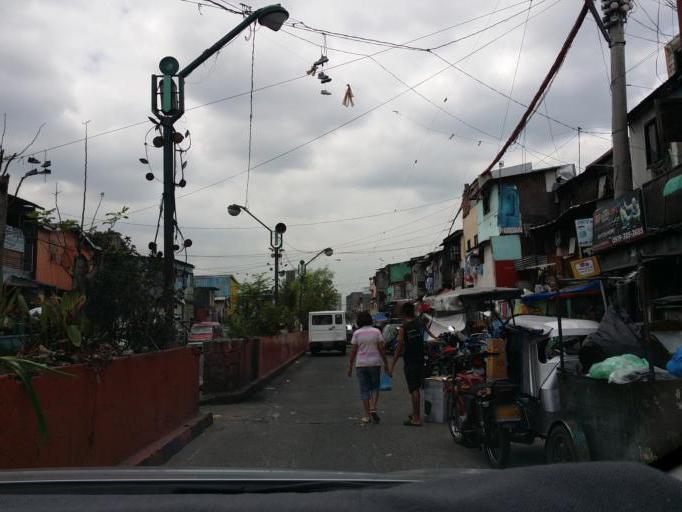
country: PH
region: Metro Manila
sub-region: Makati City
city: Makati City
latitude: 14.5713
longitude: 121.0084
